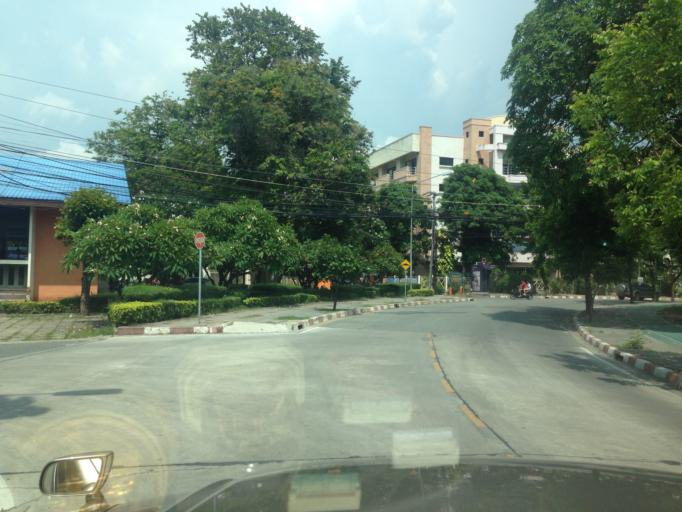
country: TH
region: Chon Buri
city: Chon Buri
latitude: 13.2777
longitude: 100.9274
